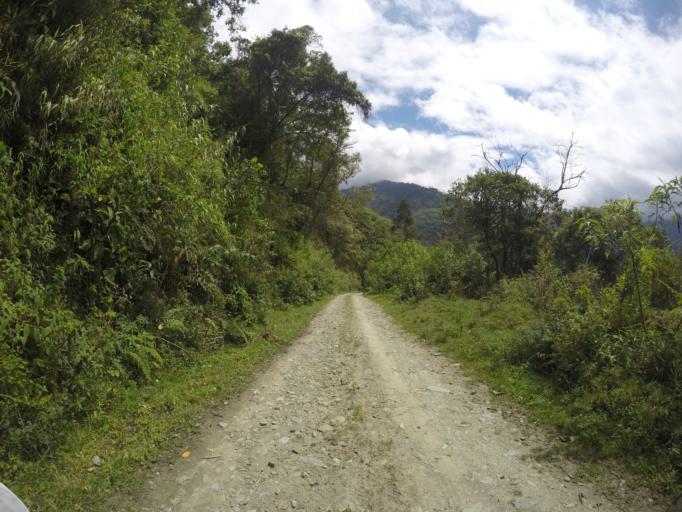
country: CO
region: Tolima
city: Cajamarca
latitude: 4.5345
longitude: -75.4199
